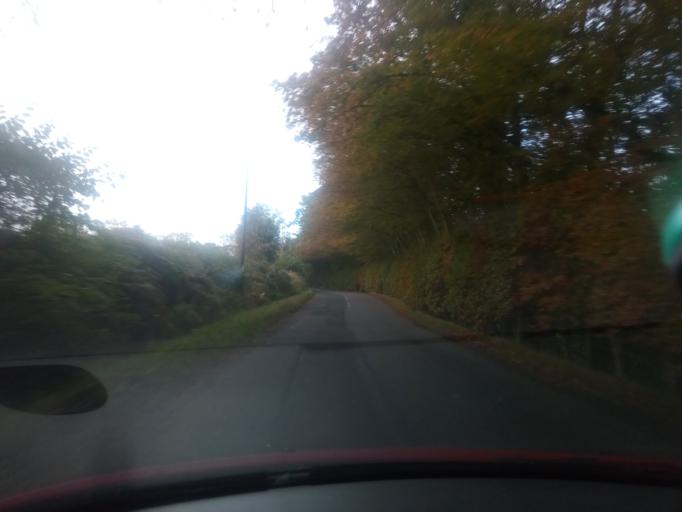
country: GB
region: Scotland
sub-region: The Scottish Borders
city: Jedburgh
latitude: 55.4501
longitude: -2.5697
